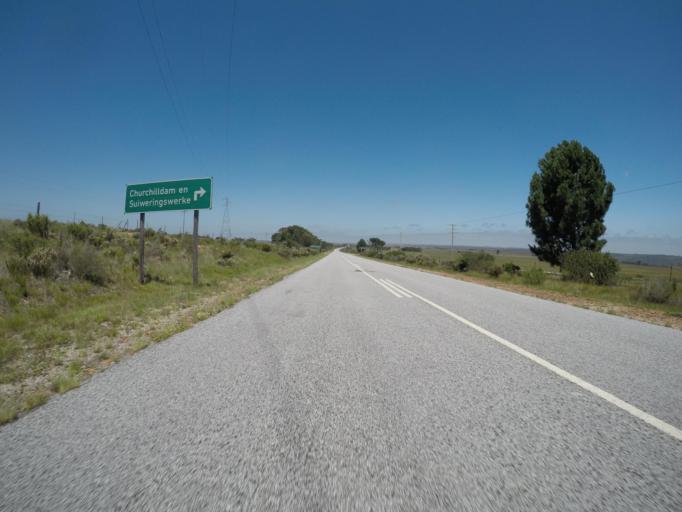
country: ZA
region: Eastern Cape
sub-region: Cacadu District Municipality
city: Kruisfontein
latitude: -34.0001
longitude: 24.5451
